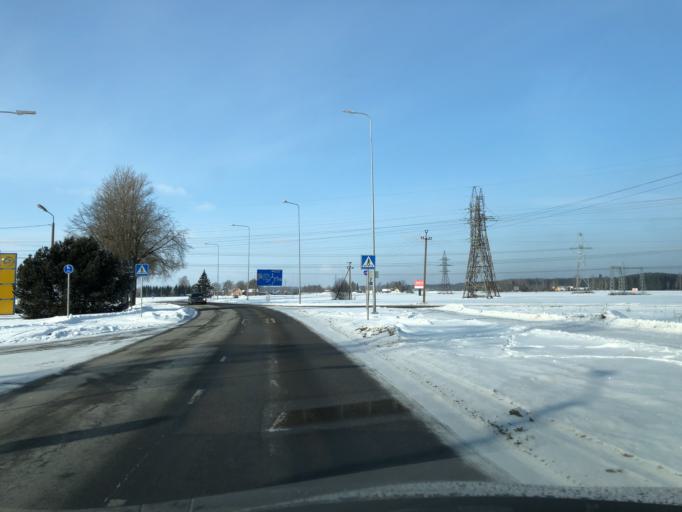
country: EE
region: Tartu
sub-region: Tartu linn
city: Tartu
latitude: 58.3789
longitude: 26.6803
